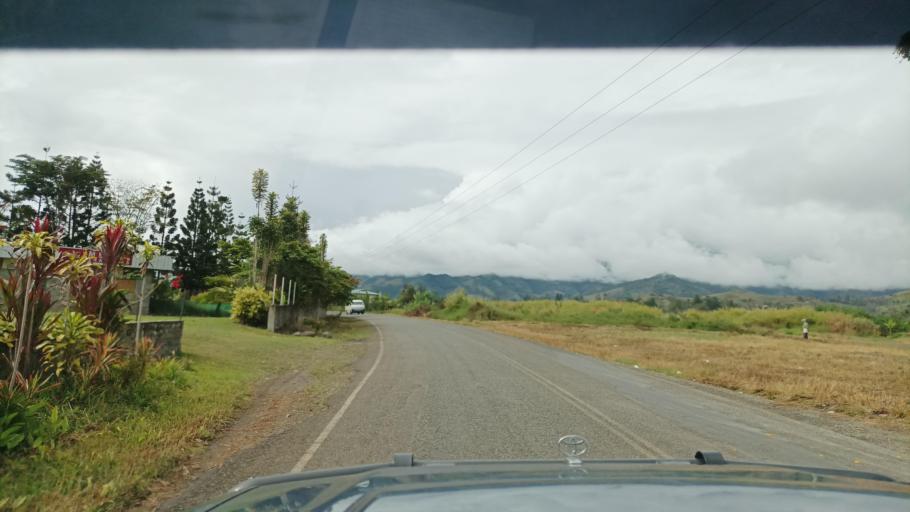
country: PG
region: Jiwaka
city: Minj
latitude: -5.8965
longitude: 144.6825
